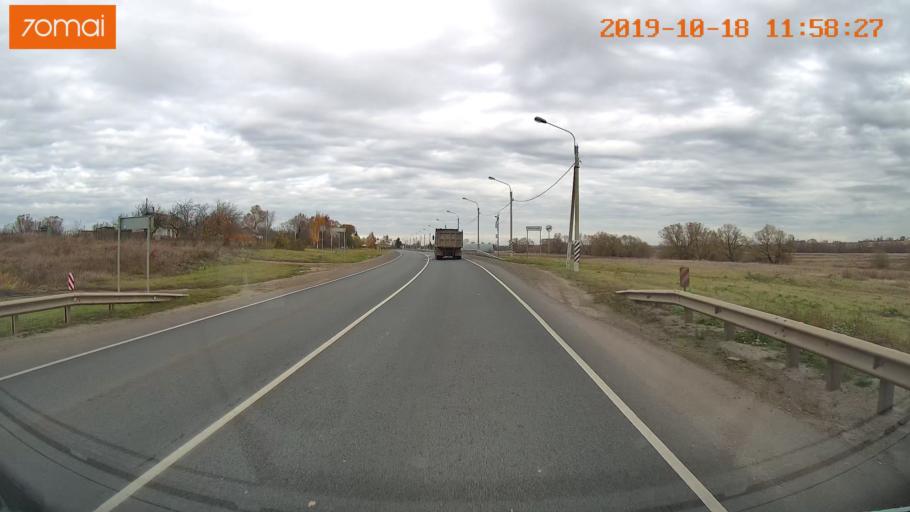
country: RU
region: Rjazan
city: Zakharovo
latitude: 54.2719
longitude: 39.1678
